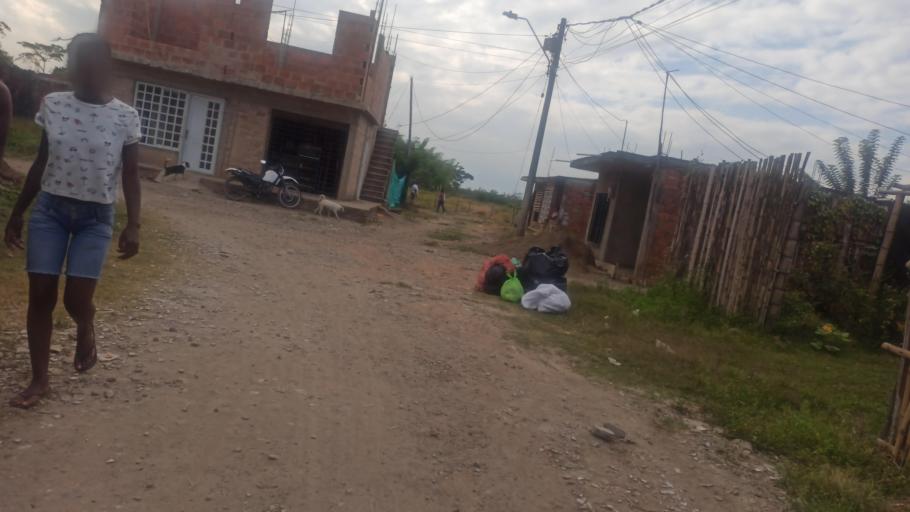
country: CO
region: Valle del Cauca
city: Jamundi
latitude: 3.1271
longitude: -76.5553
